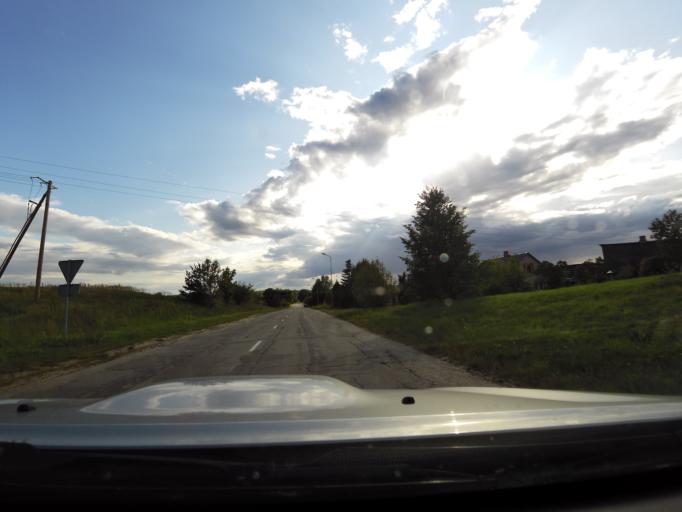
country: LV
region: Nereta
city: Nereta
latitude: 56.2117
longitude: 25.3065
